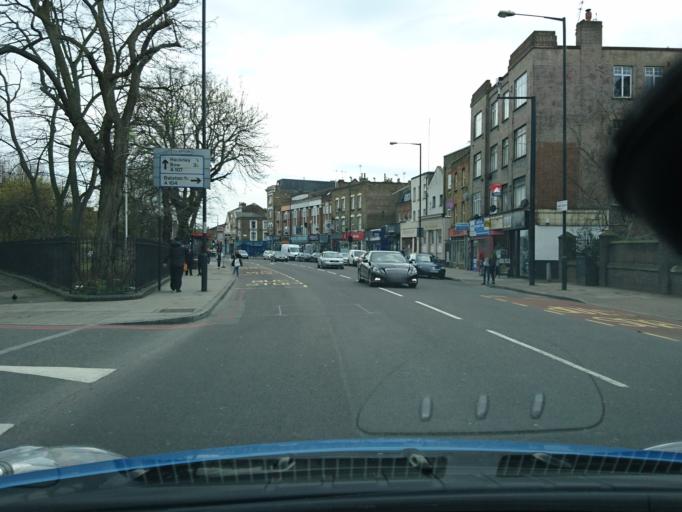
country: GB
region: England
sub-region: Greater London
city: Hackney
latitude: 51.5573
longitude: -0.0558
